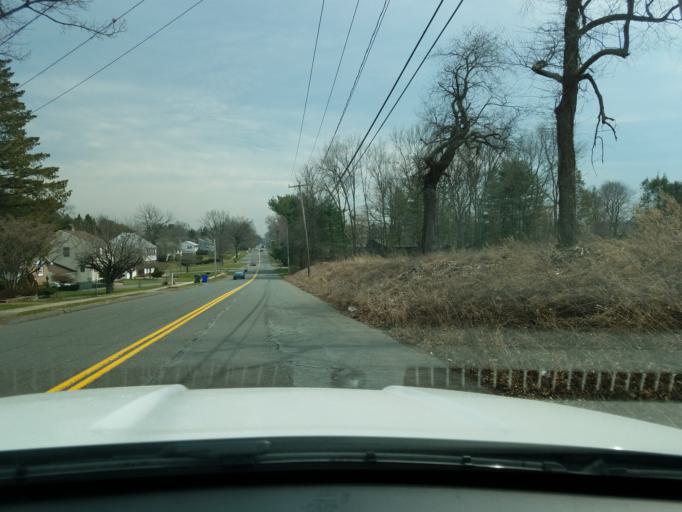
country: US
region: Connecticut
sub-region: Hartford County
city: Newington
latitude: 41.6817
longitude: -72.6908
